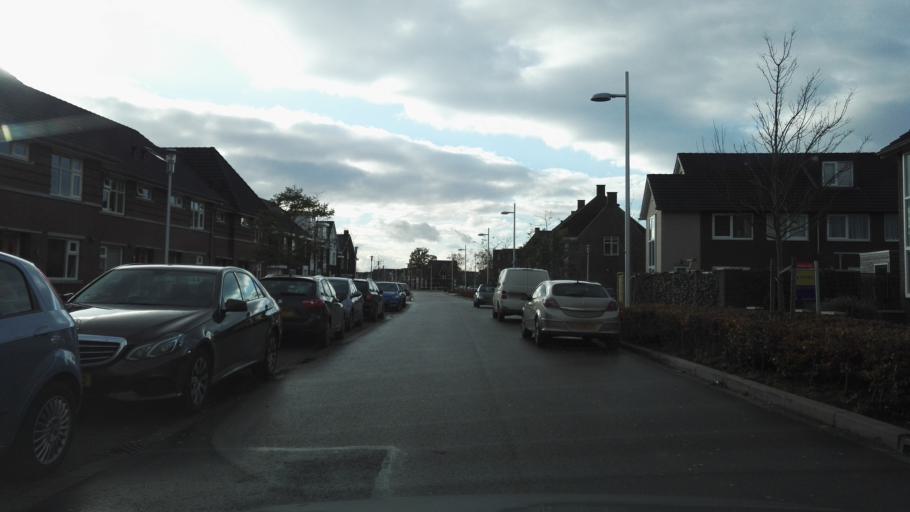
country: NL
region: Gelderland
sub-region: Gemeente Apeldoorn
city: Apeldoorn
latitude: 52.2396
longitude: 6.0020
